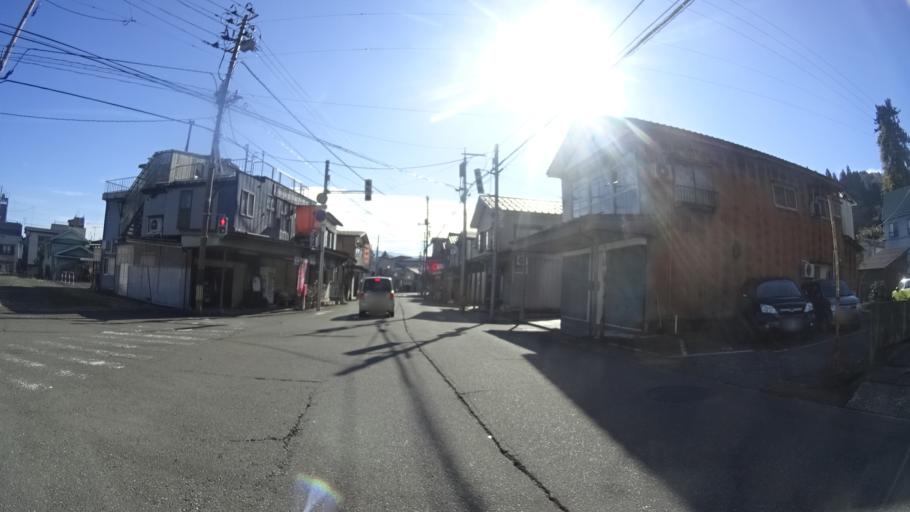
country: JP
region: Niigata
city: Tochio-honcho
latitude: 37.4800
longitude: 138.9905
